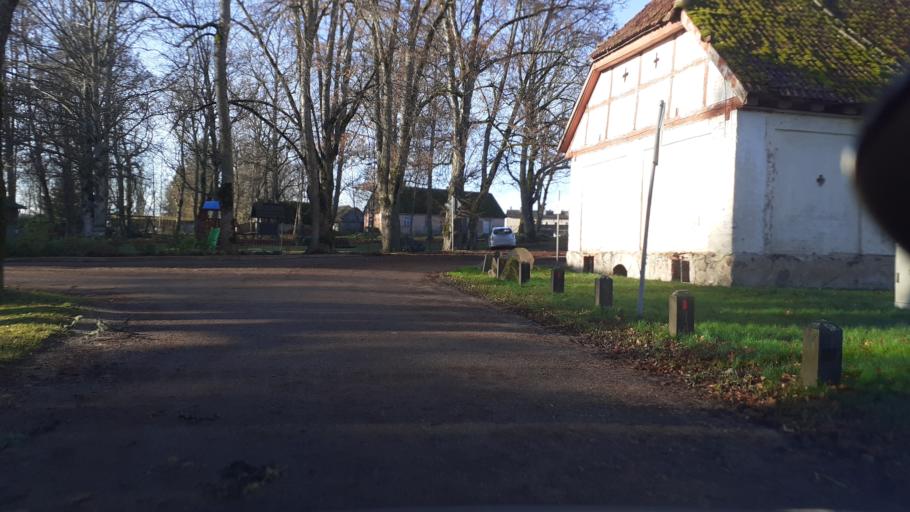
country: LV
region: Kuldigas Rajons
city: Kuldiga
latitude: 56.9998
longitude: 21.8879
